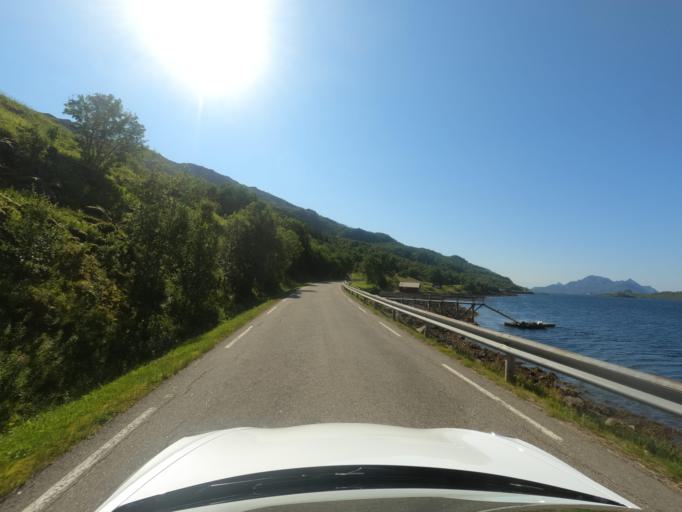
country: NO
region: Nordland
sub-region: Hadsel
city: Stokmarknes
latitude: 68.3832
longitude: 15.0898
